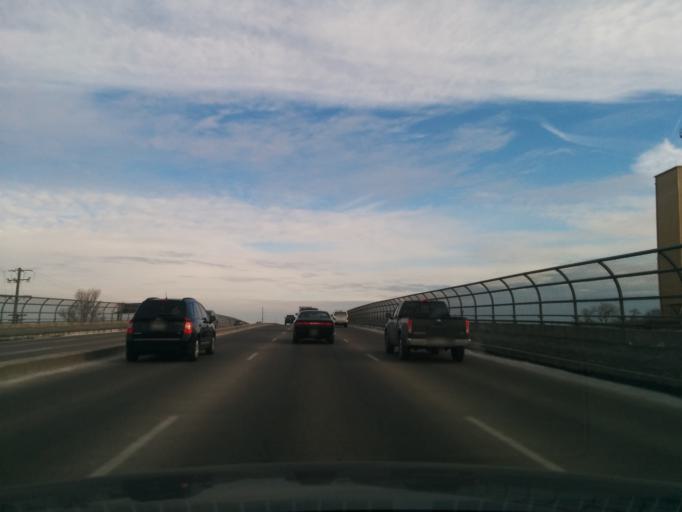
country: US
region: Illinois
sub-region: Cook County
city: Franklin Park
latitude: 41.9404
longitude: -87.8851
